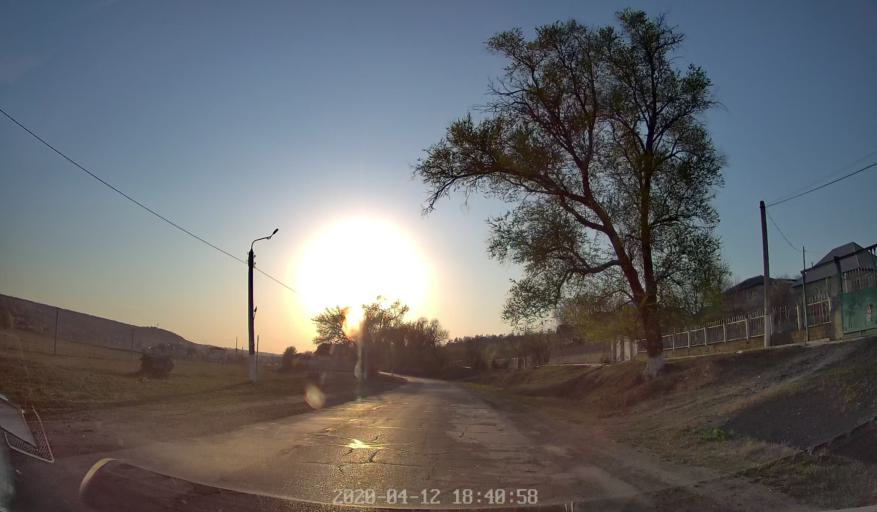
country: MD
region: Chisinau
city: Ciorescu
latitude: 47.1356
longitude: 28.9594
